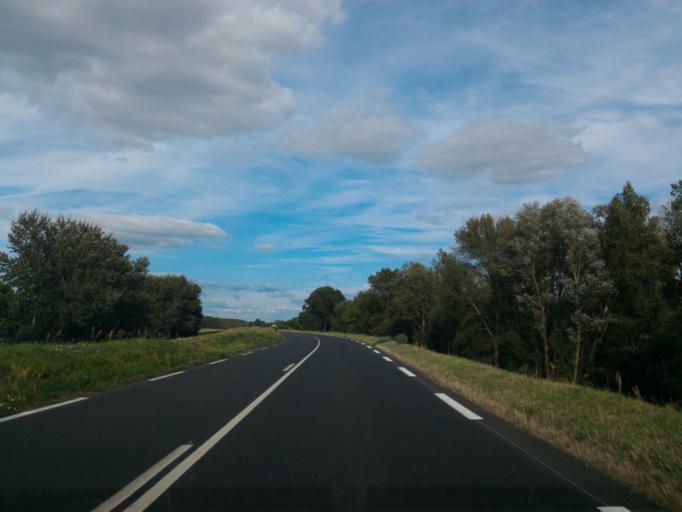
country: FR
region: Centre
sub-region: Departement du Loir-et-Cher
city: Onzain
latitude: 47.4803
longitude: 1.1613
